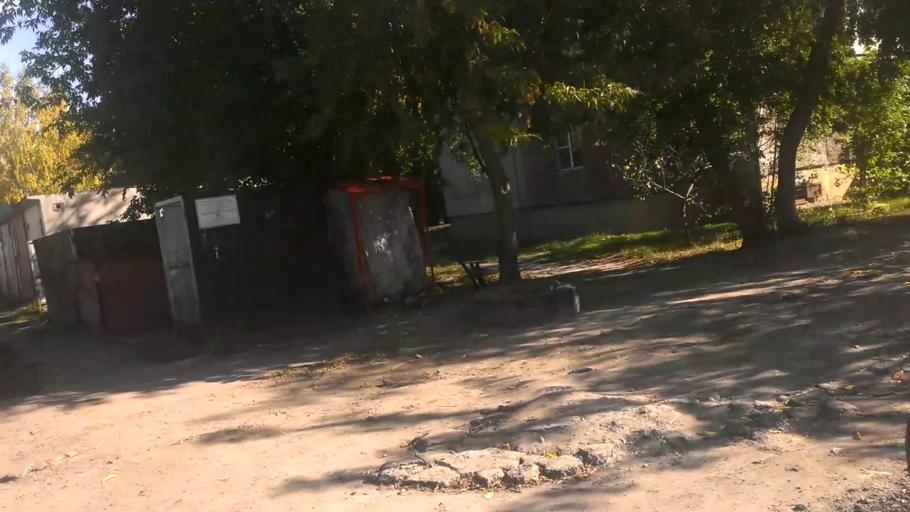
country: RU
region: Altai Krai
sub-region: Gorod Barnaulskiy
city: Barnaul
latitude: 53.3731
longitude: 83.6846
